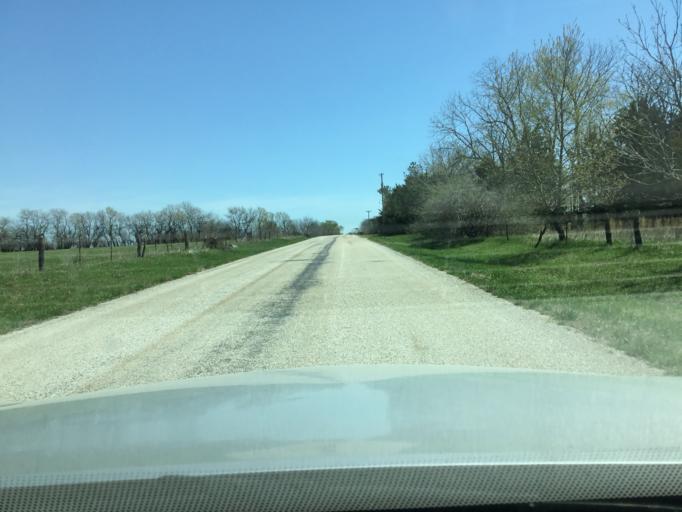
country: US
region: Kansas
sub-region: Miami County
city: Osawatomie
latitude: 38.2876
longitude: -95.0188
